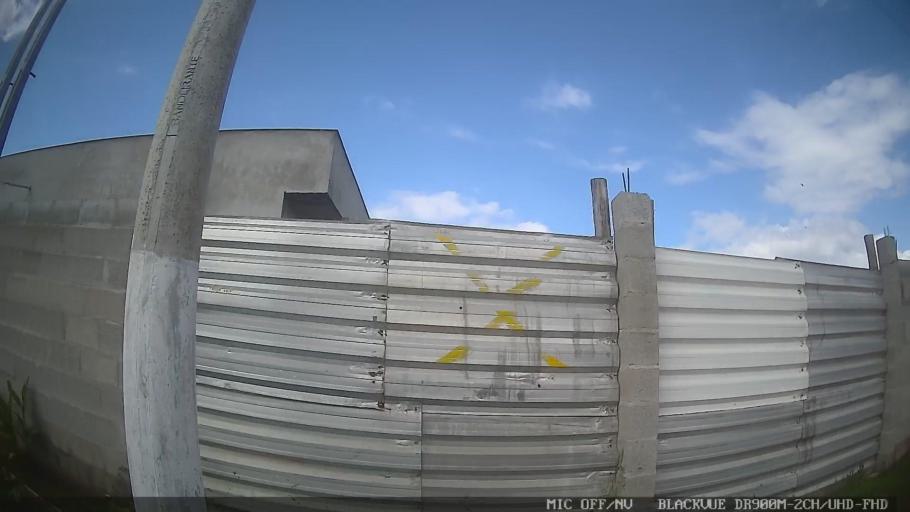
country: BR
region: Sao Paulo
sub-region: Sao Sebastiao
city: Sao Sebastiao
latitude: -23.7165
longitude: -45.4255
